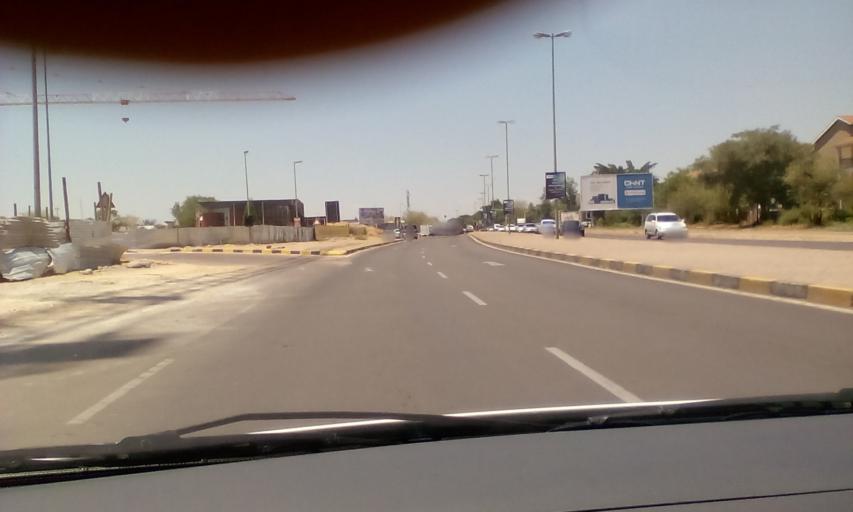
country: BW
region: South East
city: Gaborone
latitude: -24.6527
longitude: 25.9019
